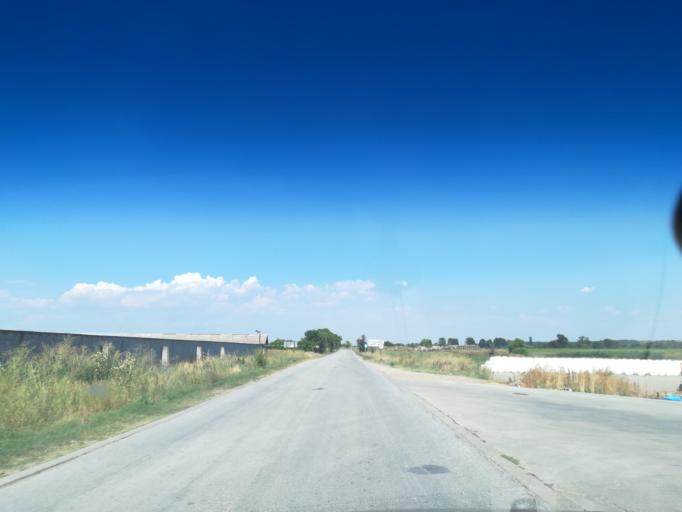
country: BG
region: Plovdiv
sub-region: Obshtina Sadovo
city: Sadovo
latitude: 42.0337
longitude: 25.1200
